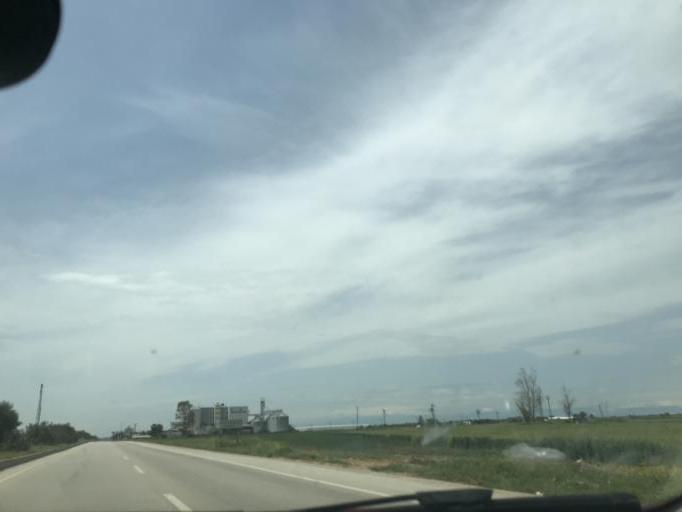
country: TR
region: Adana
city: Yakapinar
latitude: 36.9738
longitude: 35.5021
